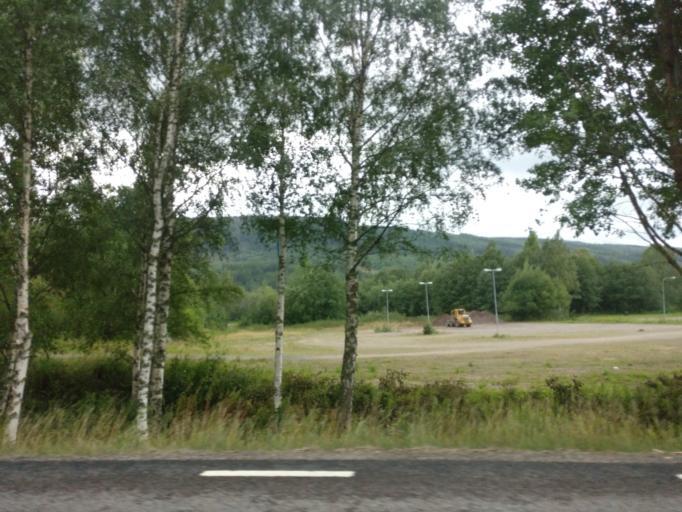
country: SE
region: Vaermland
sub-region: Torsby Kommun
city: Torsby
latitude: 60.7355
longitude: 12.8650
